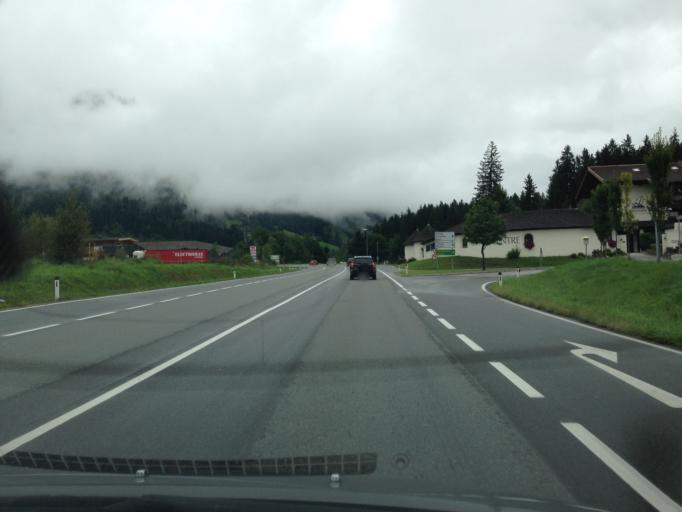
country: AT
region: Salzburg
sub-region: Politischer Bezirk Zell am See
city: Maishofen
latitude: 47.3904
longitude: 12.8035
